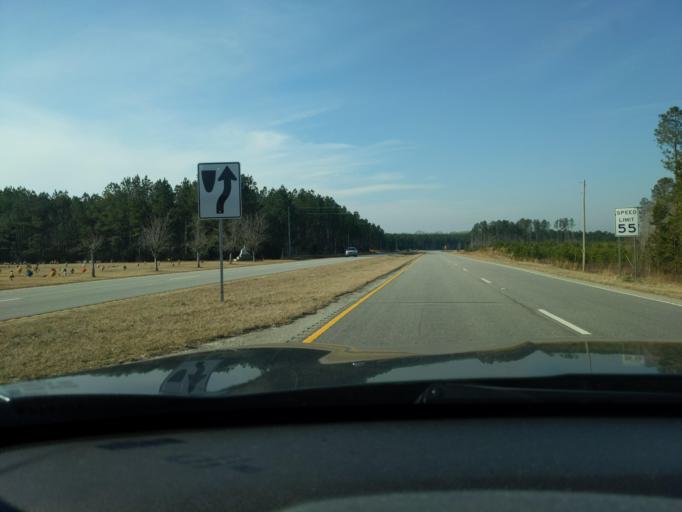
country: US
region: South Carolina
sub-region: Abbeville County
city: Abbeville
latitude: 34.1165
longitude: -82.4633
